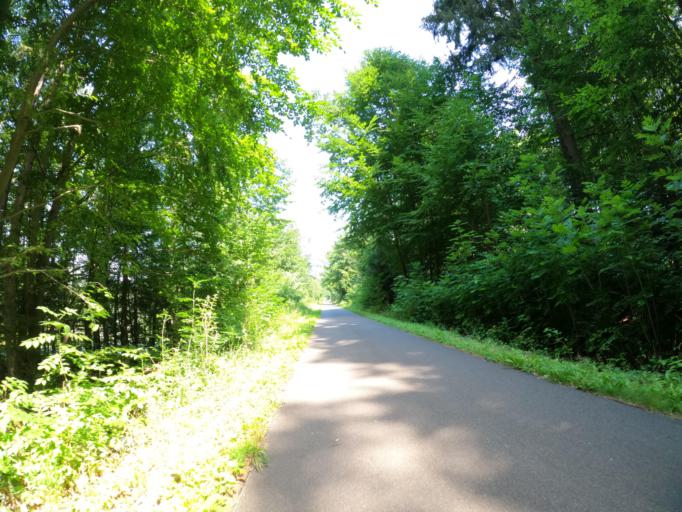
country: DE
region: Brandenburg
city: Templin
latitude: 53.2424
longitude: 13.5046
